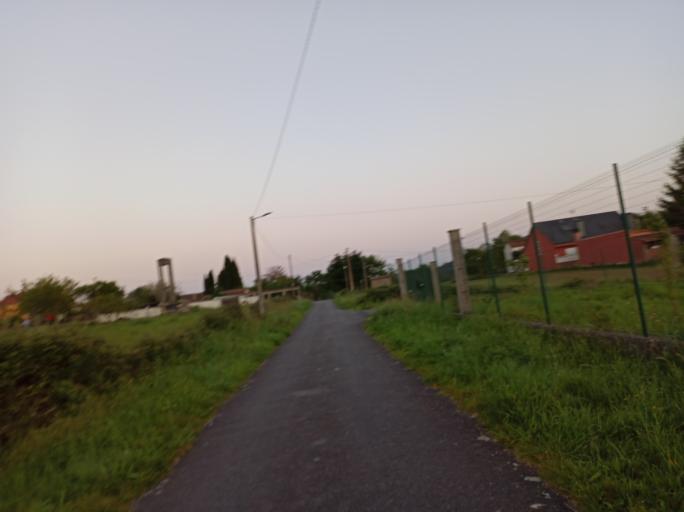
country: ES
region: Galicia
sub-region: Provincia da Coruna
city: Negreira
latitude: 42.9101
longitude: -8.7430
